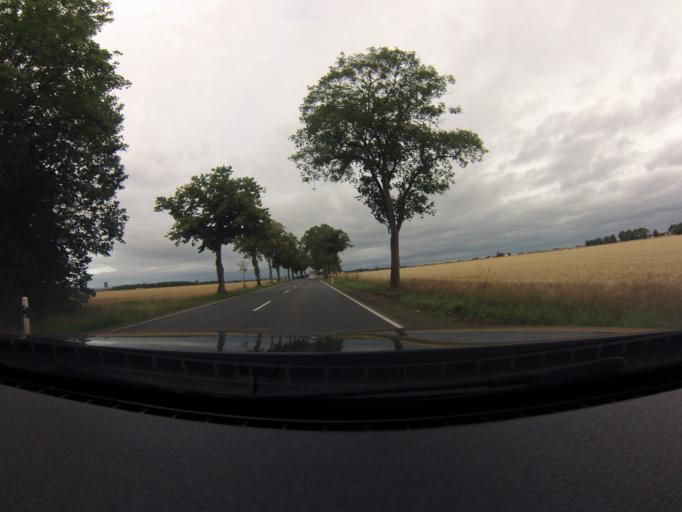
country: DE
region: North Rhine-Westphalia
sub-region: Regierungsbezirk Koln
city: Rheinbach
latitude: 50.6781
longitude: 6.9491
